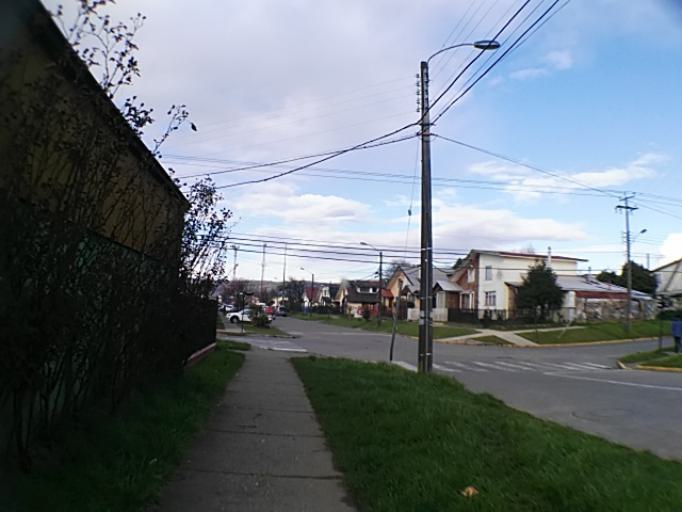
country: CL
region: Los Lagos
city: Las Animas
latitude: -39.8340
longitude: -73.2231
